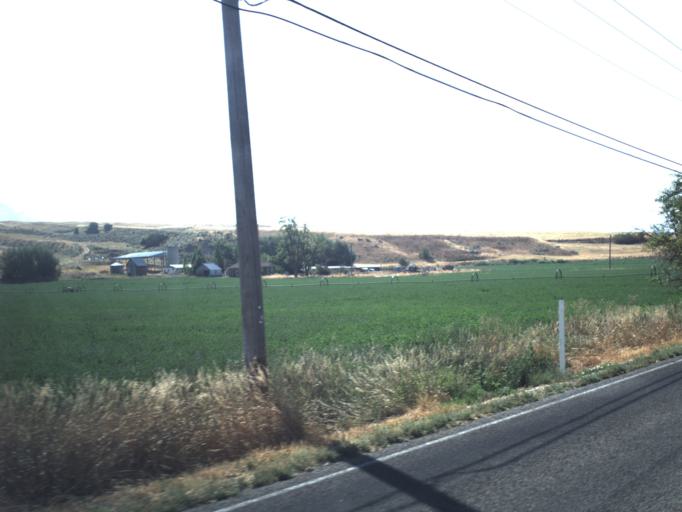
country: US
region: Utah
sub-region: Cache County
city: Hyrum
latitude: 41.6025
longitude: -111.8337
